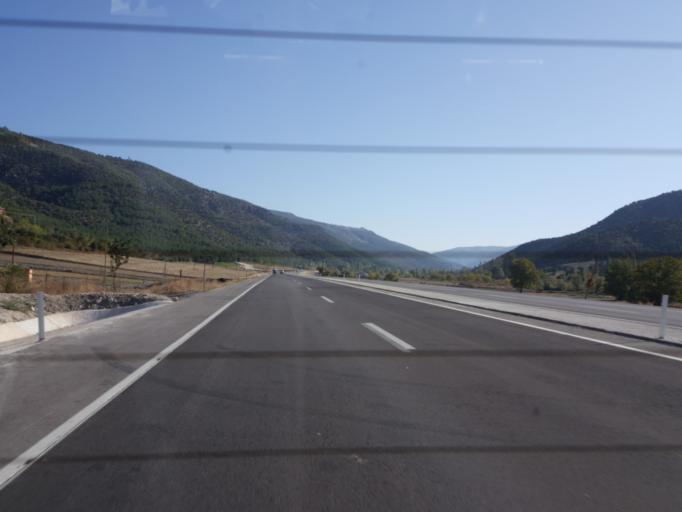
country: TR
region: Tokat
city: Turhal
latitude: 40.4661
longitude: 36.1205
